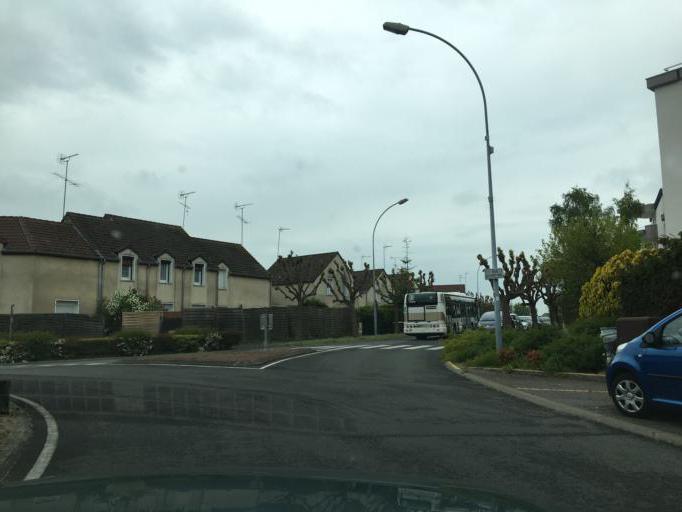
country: FR
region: Centre
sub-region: Departement du Loiret
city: Saran
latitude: 47.9320
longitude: 1.8893
